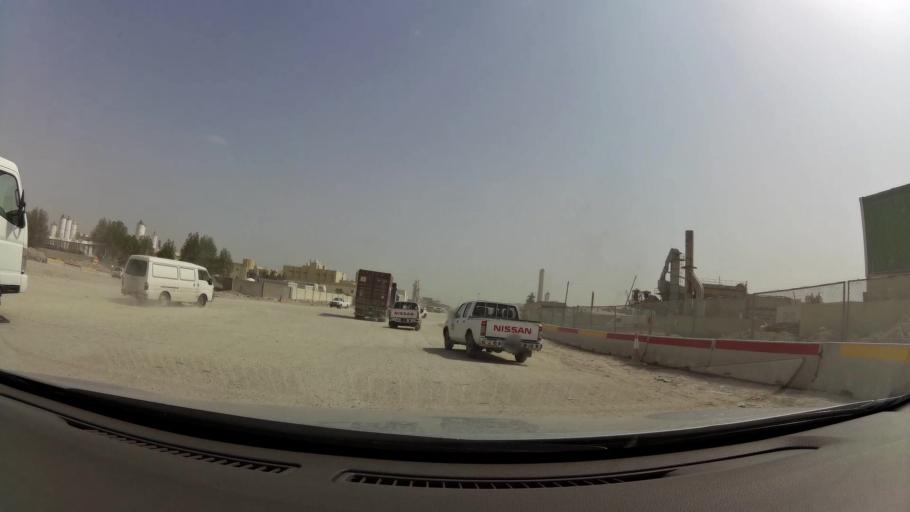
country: QA
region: Al Wakrah
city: Al Wukayr
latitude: 25.1733
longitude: 51.4415
